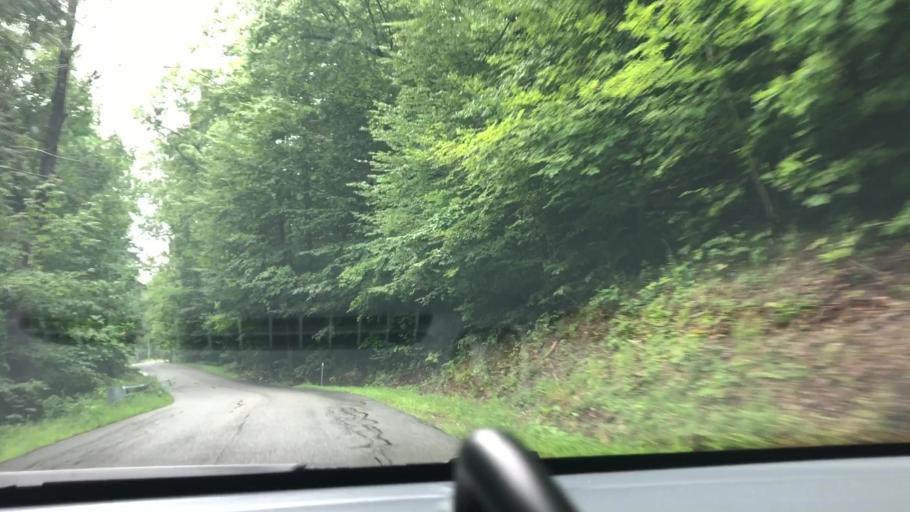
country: US
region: New Hampshire
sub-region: Hillsborough County
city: Pinardville
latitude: 42.9815
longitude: -71.5333
